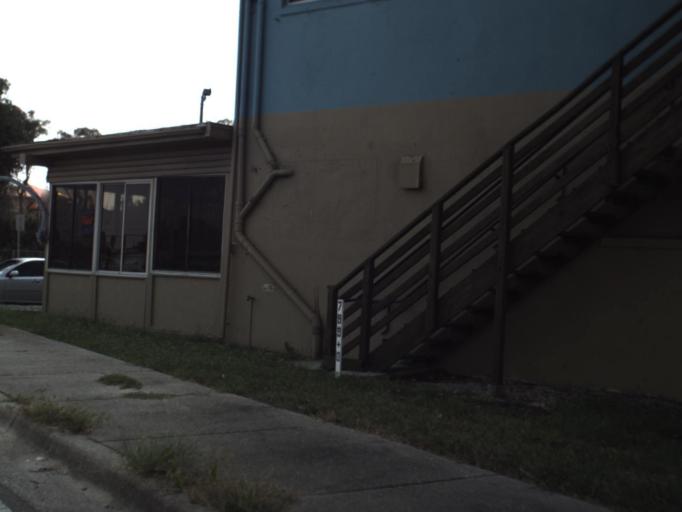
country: US
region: Florida
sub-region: Pinellas County
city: Gandy
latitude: 27.8643
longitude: -82.6373
